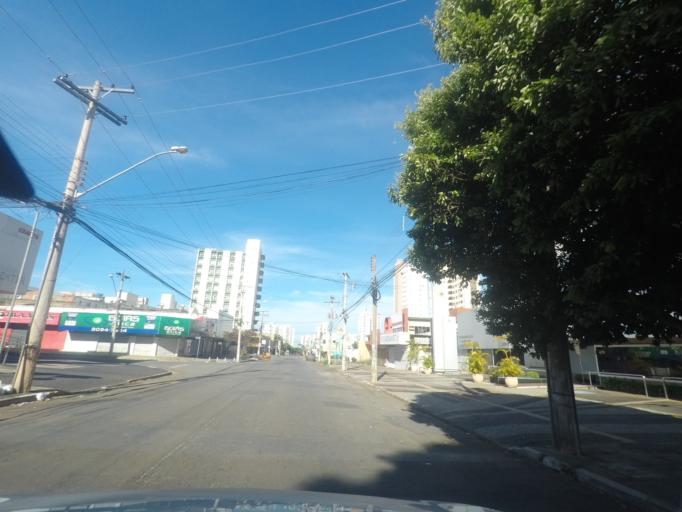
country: BR
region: Goias
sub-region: Goiania
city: Goiania
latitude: -16.6753
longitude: -49.2689
